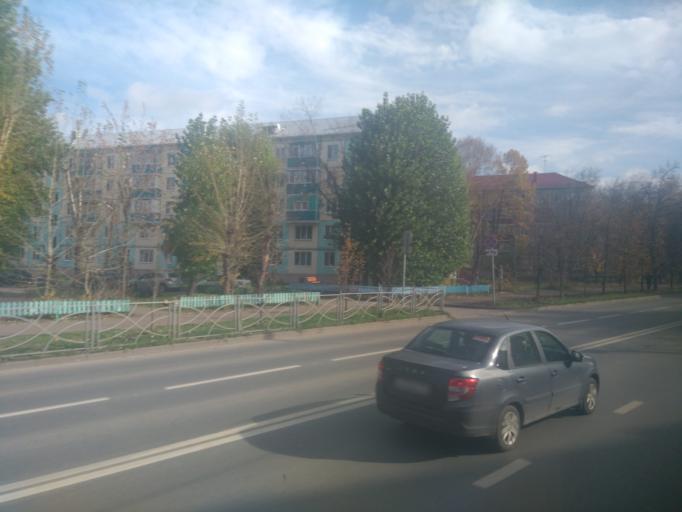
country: RU
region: Tatarstan
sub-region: Gorod Kazan'
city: Kazan
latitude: 55.8016
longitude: 49.1872
